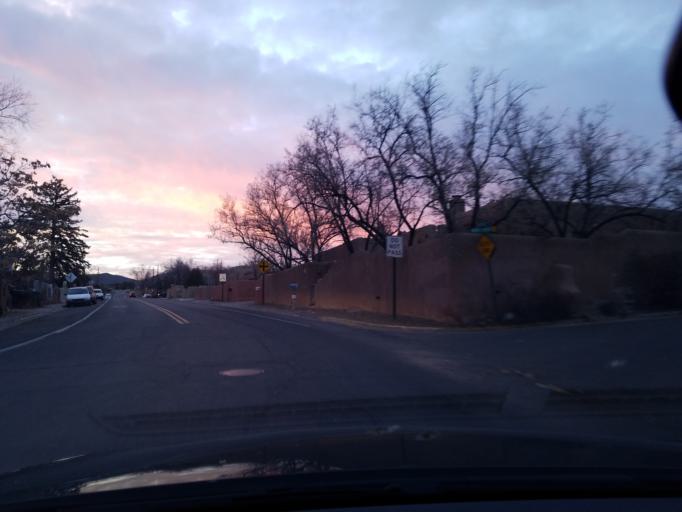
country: US
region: New Mexico
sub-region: Santa Fe County
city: Santa Fe
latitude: 35.6930
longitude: -105.9340
